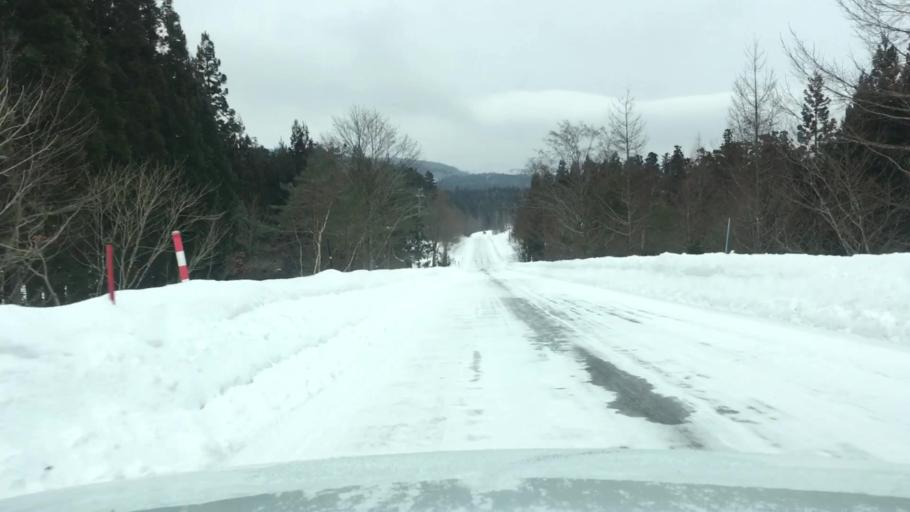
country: JP
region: Akita
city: Hanawa
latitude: 39.9858
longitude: 141.0017
